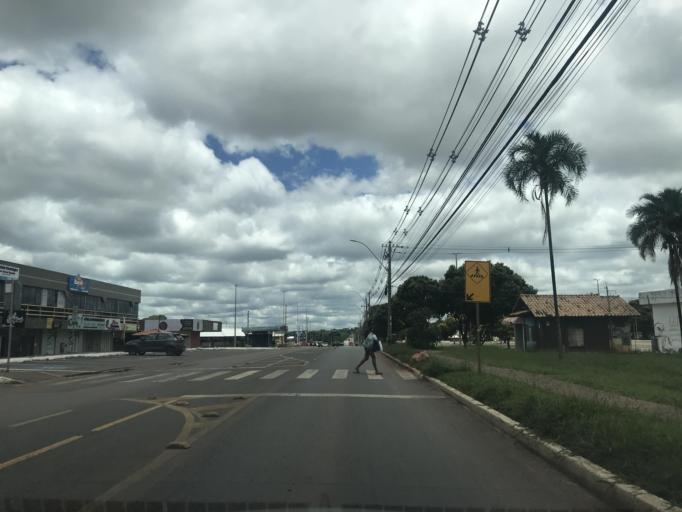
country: BR
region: Federal District
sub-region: Brasilia
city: Brasilia
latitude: -15.6512
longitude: -47.7873
